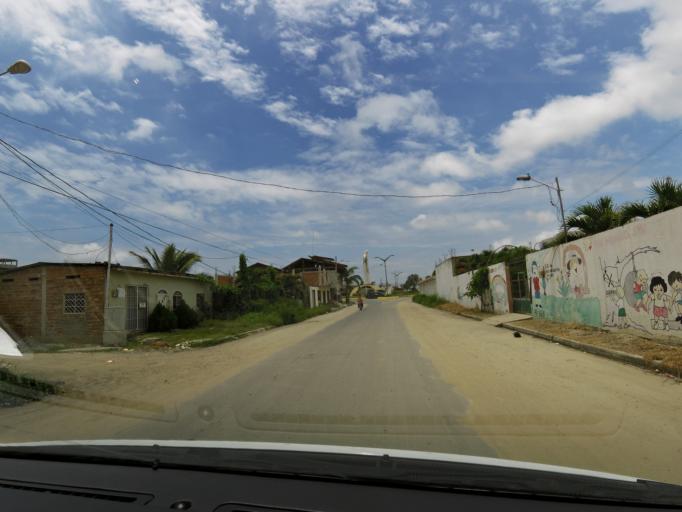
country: EC
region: El Oro
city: Huaquillas
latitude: -3.4855
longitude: -80.2157
